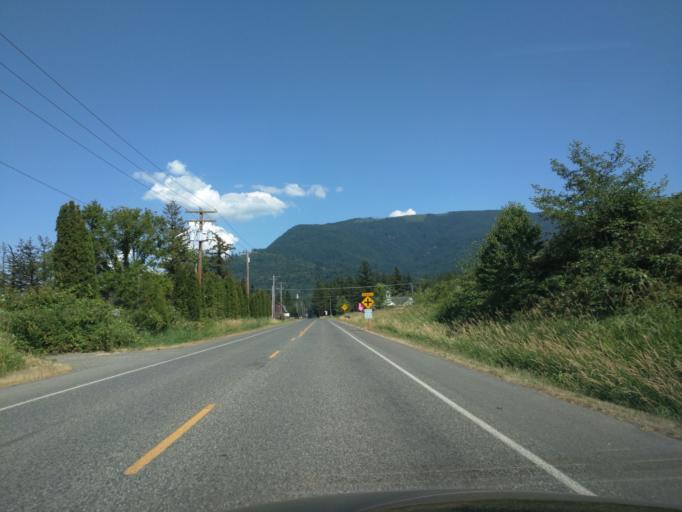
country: US
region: Washington
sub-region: Whatcom County
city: Nooksack
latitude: 48.9202
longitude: -122.2906
